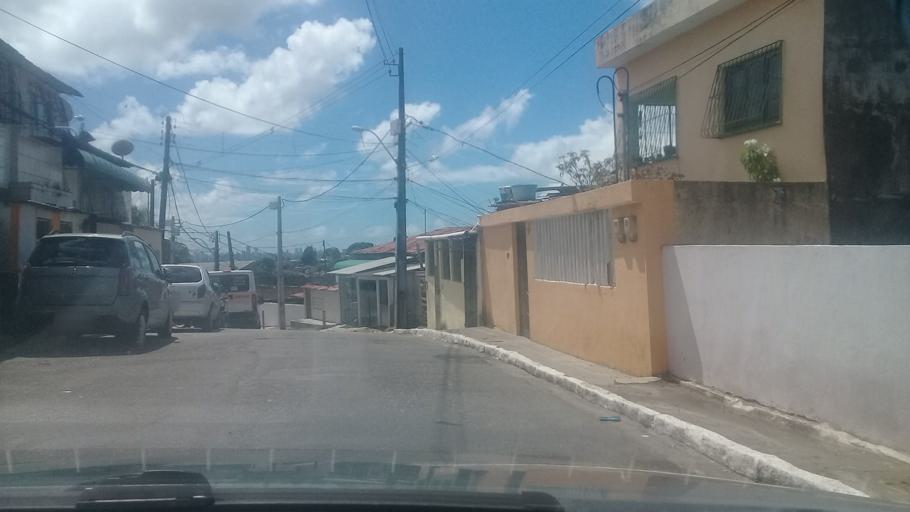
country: BR
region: Pernambuco
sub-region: Jaboatao Dos Guararapes
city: Jaboatao dos Guararapes
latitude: -8.1243
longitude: -34.9464
